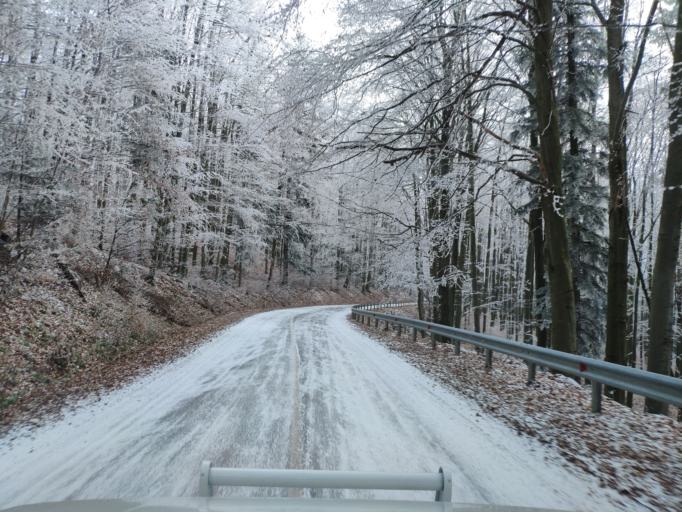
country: SK
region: Kosicky
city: Dobsina
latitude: 48.8046
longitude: 20.4862
